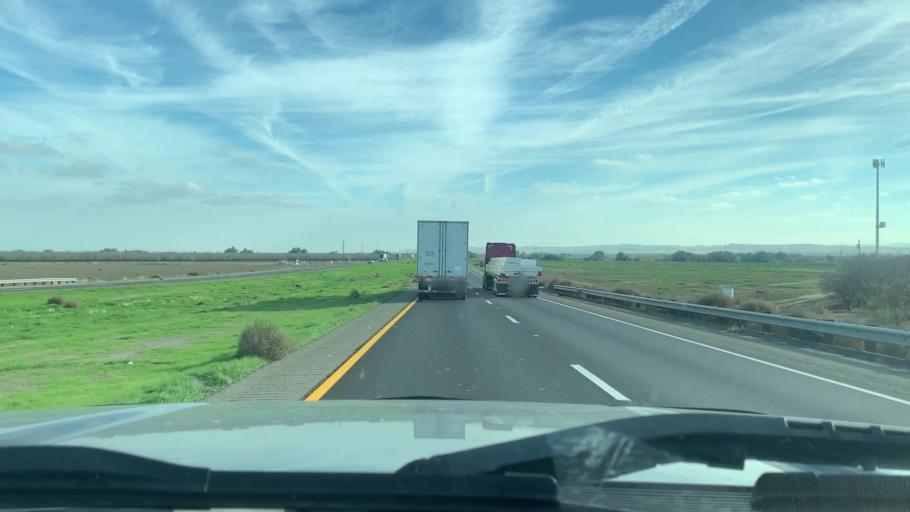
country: US
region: California
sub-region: Fresno County
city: Huron
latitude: 36.1746
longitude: -120.1928
